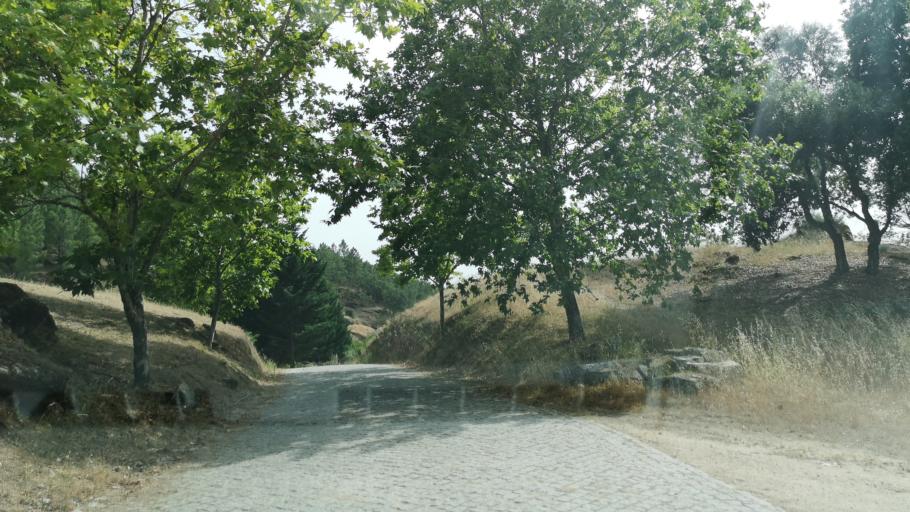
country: PT
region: Castelo Branco
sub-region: Belmonte
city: Belmonte
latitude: 40.3448
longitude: -7.3600
